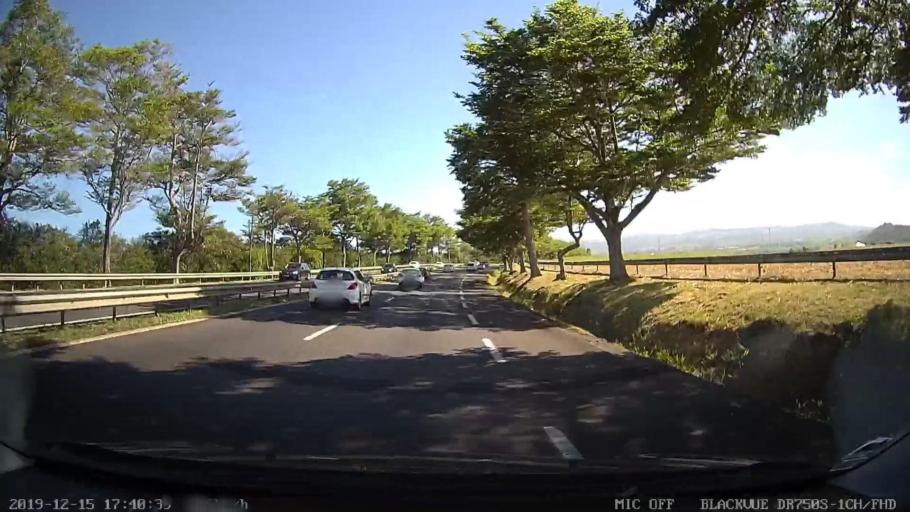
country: RE
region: Reunion
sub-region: Reunion
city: Saint-Pierre
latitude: -21.3174
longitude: 55.4906
